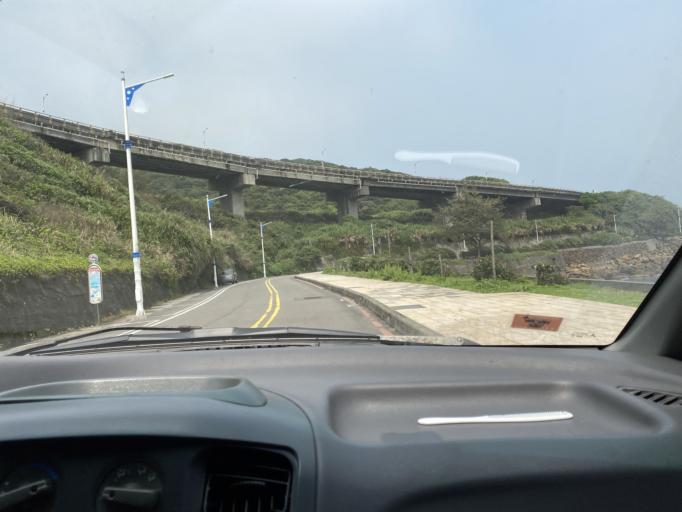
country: TW
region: Taiwan
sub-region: Keelung
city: Keelung
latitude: 25.1680
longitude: 121.7075
